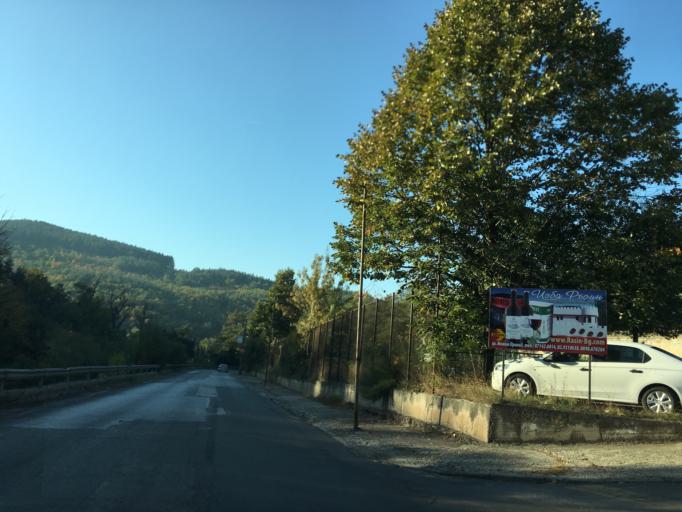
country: BG
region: Sofiya
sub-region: Obshtina Dolna Banya
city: Dolna Banya
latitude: 42.3304
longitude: 23.8710
